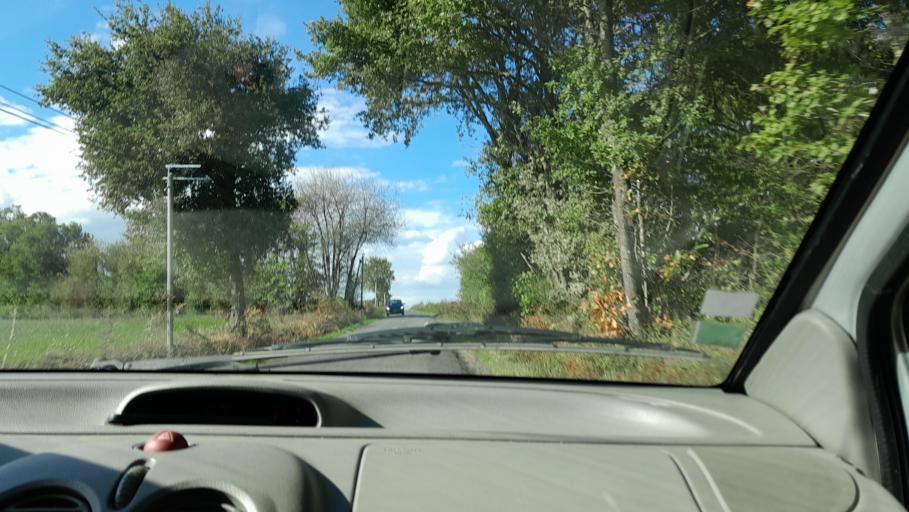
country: FR
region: Pays de la Loire
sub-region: Departement de la Mayenne
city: Ahuille
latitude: 48.0252
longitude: -0.8863
